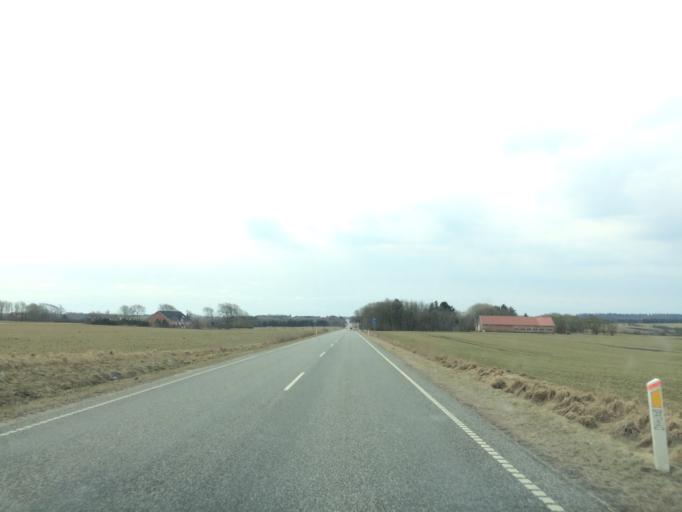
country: DK
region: Central Jutland
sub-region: Ringkobing-Skjern Kommune
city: Videbaek
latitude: 56.0738
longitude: 8.5068
